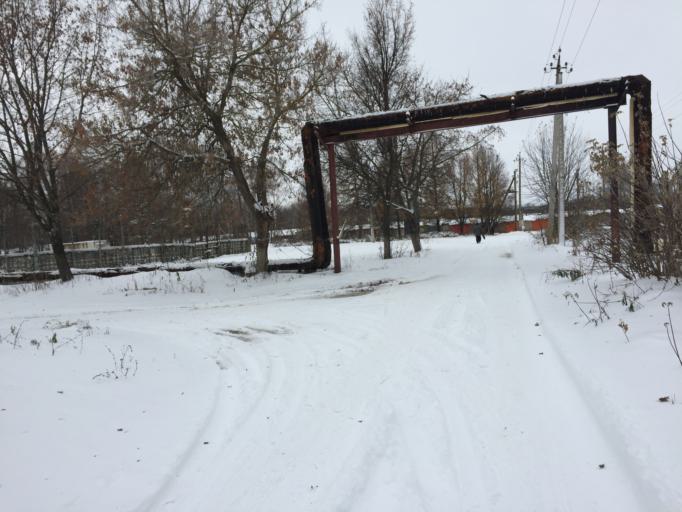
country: RU
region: Tula
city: Shchekino
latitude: 53.8524
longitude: 37.4790
